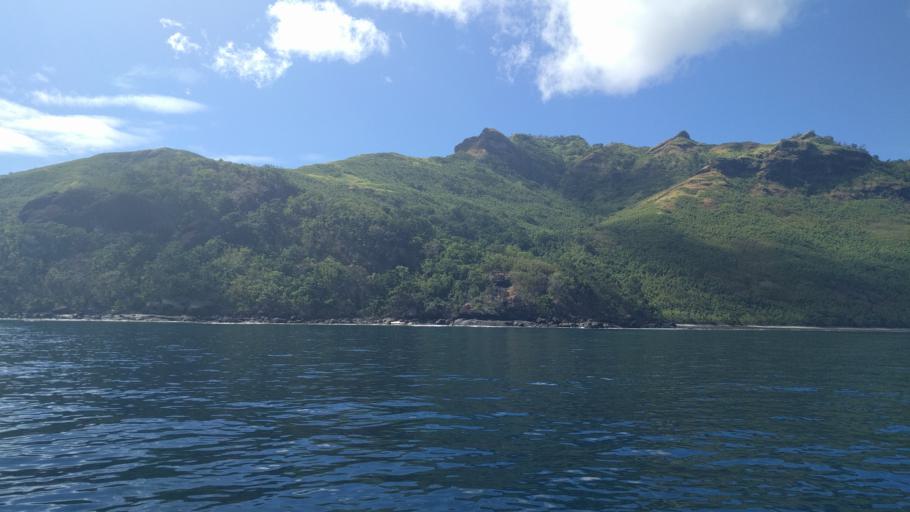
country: FJ
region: Western
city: Lautoka
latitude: -17.2911
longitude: 177.1003
